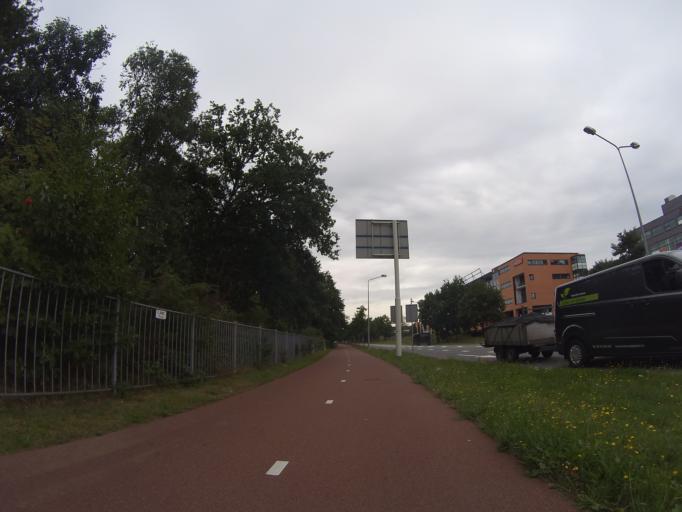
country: NL
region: North Holland
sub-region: Gemeente Hilversum
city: Hilversum
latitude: 52.2419
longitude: 5.1717
